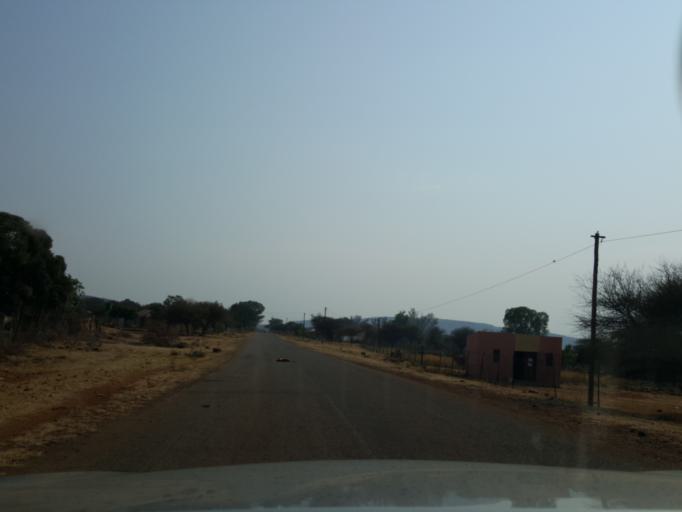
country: BW
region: South East
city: Lobatse
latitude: -25.3231
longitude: 25.7936
